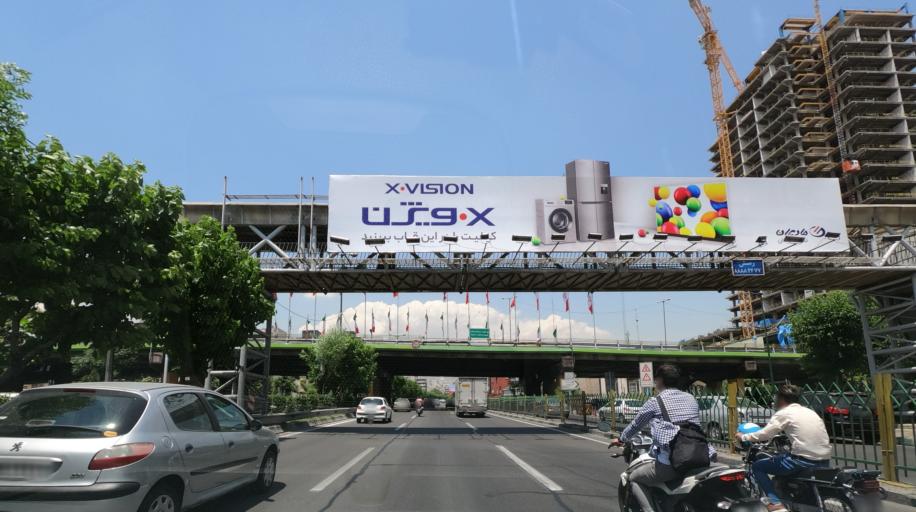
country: IR
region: Tehran
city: Tajrish
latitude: 35.7612
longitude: 51.4208
